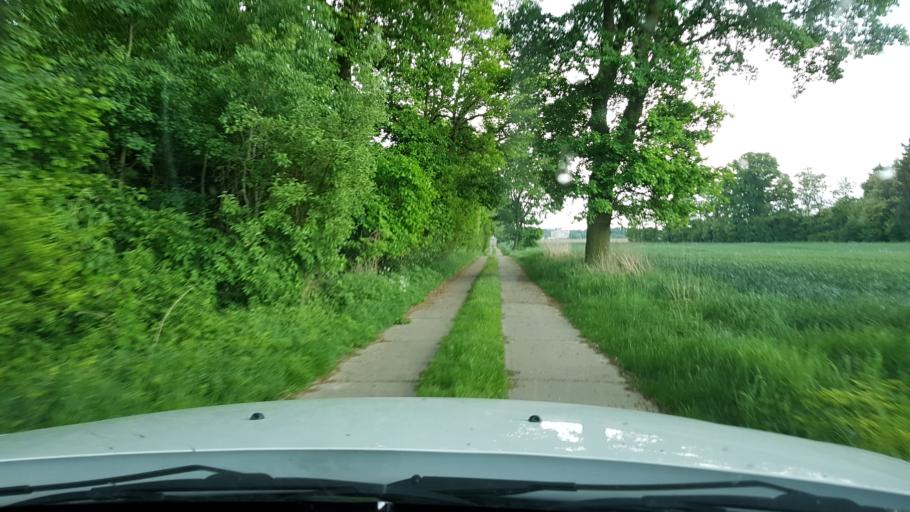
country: PL
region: West Pomeranian Voivodeship
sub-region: Powiat stargardzki
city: Stara Dabrowa
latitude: 53.3491
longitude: 15.1823
